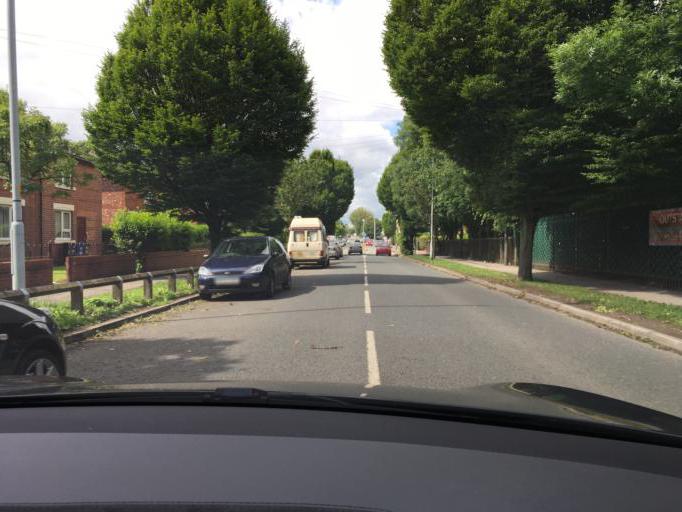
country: GB
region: England
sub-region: Borough of Stockport
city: Stockport
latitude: 53.3894
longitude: -2.1666
